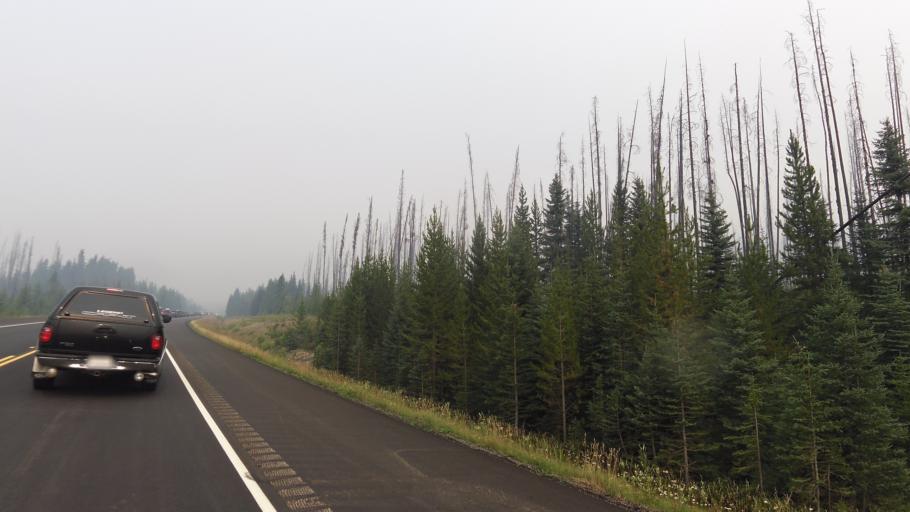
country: CA
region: Alberta
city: Lake Louise
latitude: 51.0907
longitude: -116.0650
